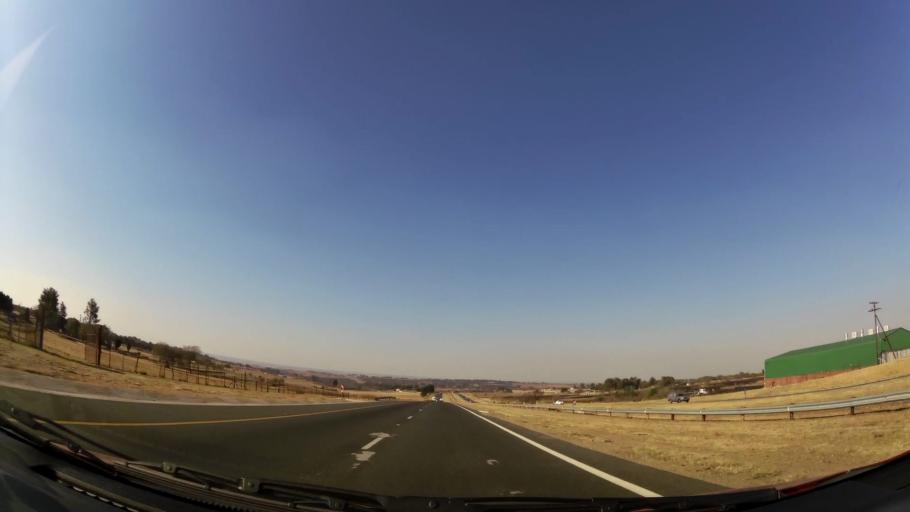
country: ZA
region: Gauteng
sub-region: West Rand District Municipality
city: Muldersdriseloop
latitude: -26.0116
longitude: 27.8821
